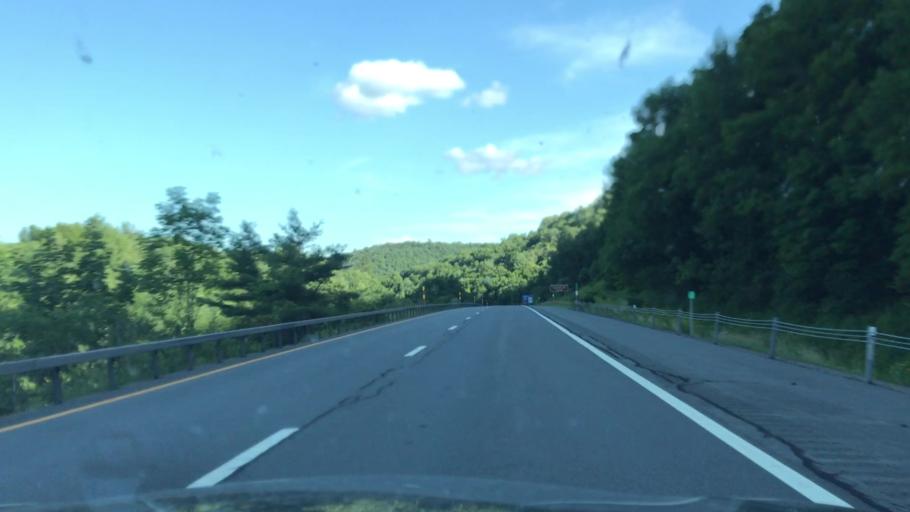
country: US
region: New York
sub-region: Sullivan County
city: Livingston Manor
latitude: 41.9419
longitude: -74.9299
